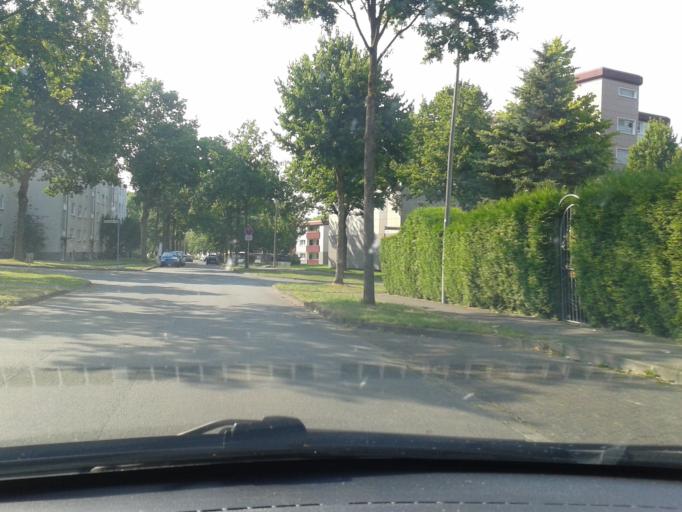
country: DE
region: North Rhine-Westphalia
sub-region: Regierungsbezirk Detmold
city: Paderborn
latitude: 51.7080
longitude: 8.7892
